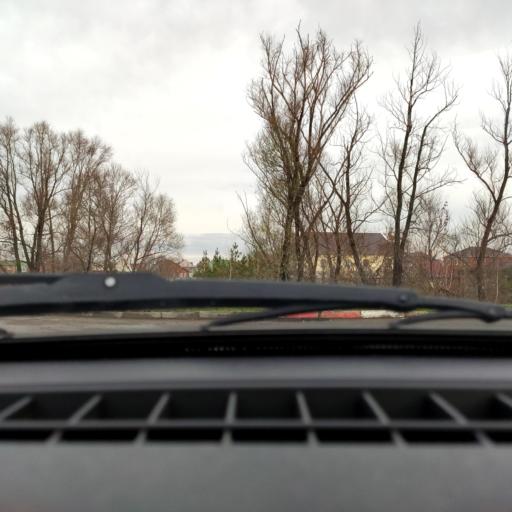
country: RU
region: Bashkortostan
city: Ufa
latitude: 54.6471
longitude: 55.9208
